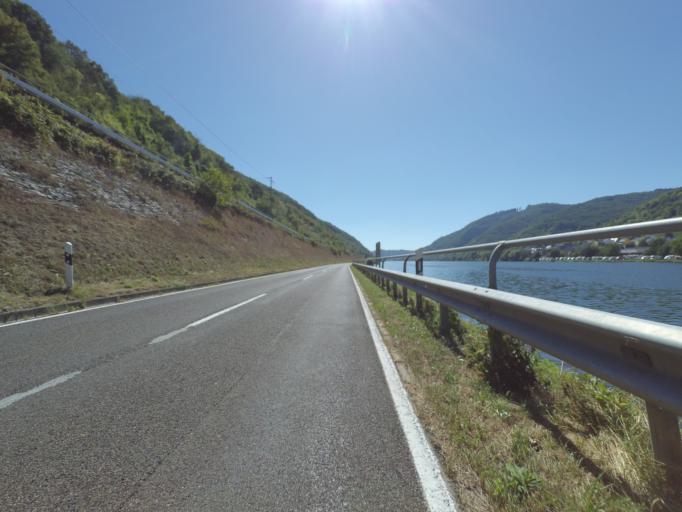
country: DE
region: Rheinland-Pfalz
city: Sankt Aldegund
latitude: 50.0812
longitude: 7.1341
